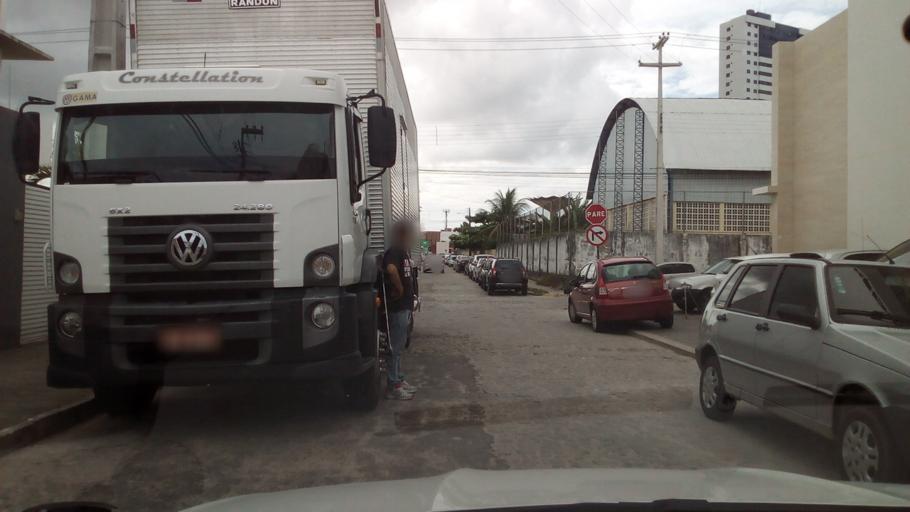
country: BR
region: Paraiba
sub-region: Joao Pessoa
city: Joao Pessoa
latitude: -7.1226
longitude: -34.8596
